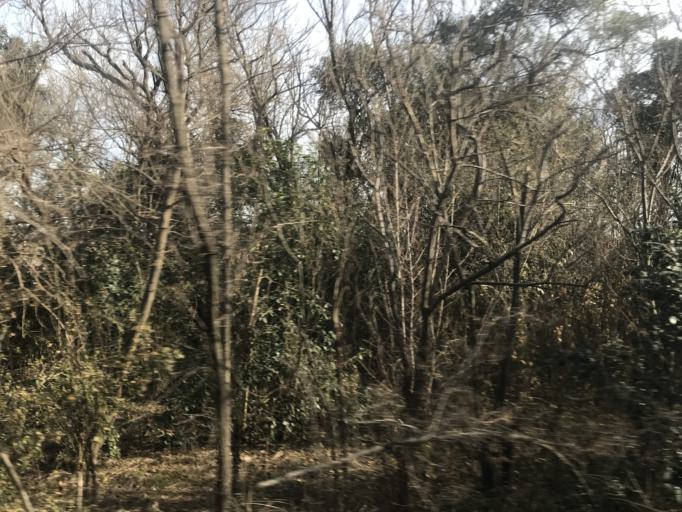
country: AR
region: Cordoba
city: Laguna Larga
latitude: -31.7632
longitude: -63.8148
